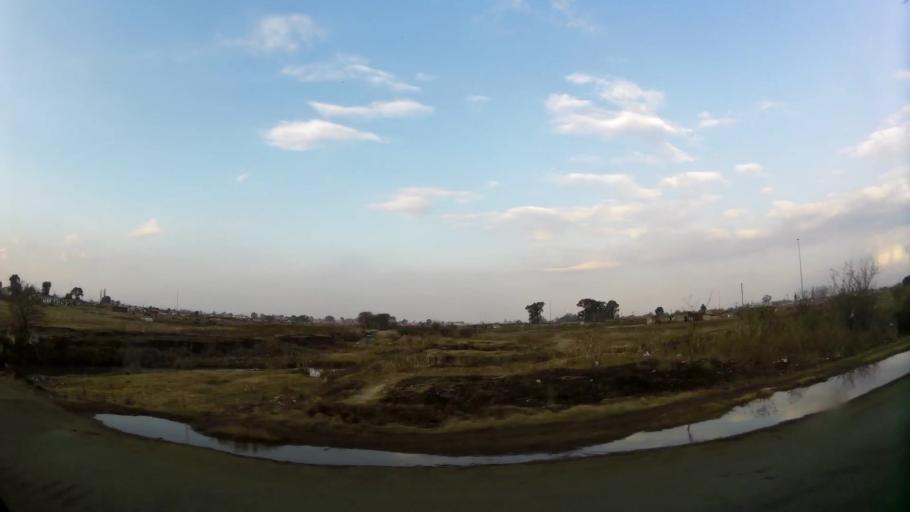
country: ZA
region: Gauteng
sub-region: City of Johannesburg Metropolitan Municipality
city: Orange Farm
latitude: -26.5440
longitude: 27.8331
